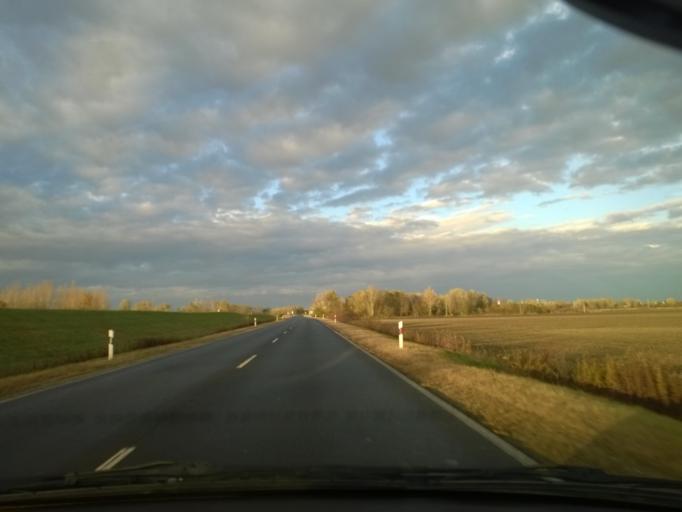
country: HU
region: Bacs-Kiskun
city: Harta
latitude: 46.6810
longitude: 19.0150
